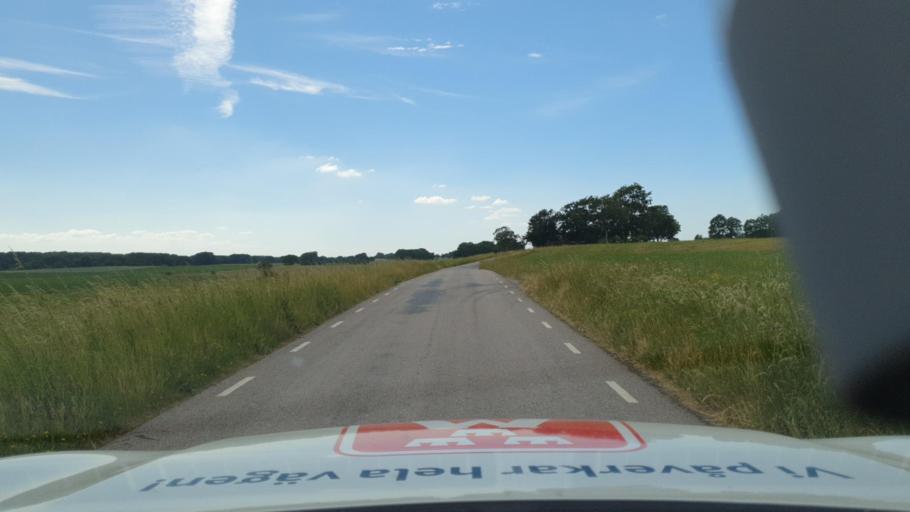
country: SE
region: Skane
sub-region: Sjobo Kommun
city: Sjoebo
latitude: 55.6293
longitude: 13.8382
